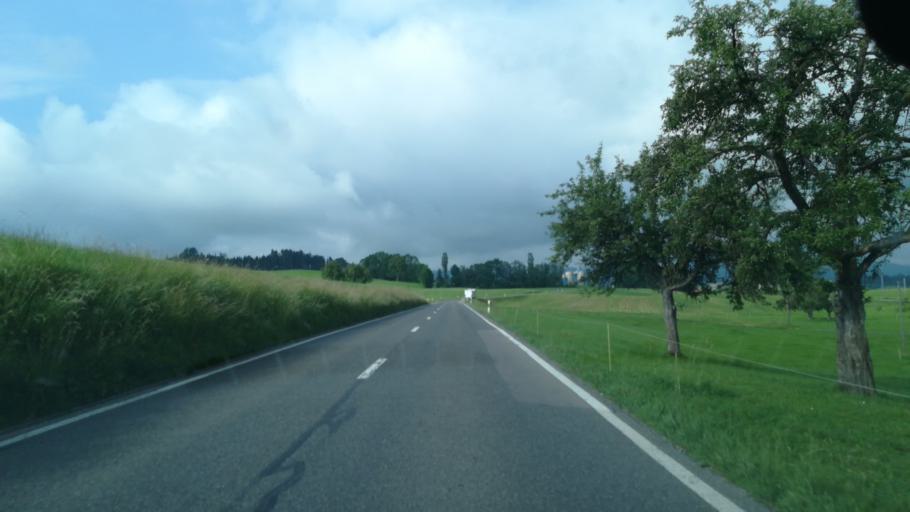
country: CH
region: Saint Gallen
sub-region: Wahlkreis St. Gallen
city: Gossau
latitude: 47.4362
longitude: 9.2513
